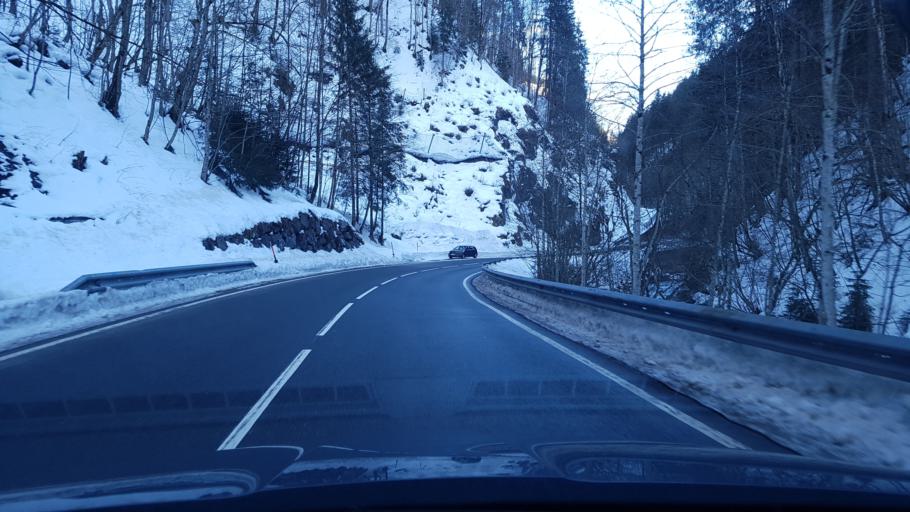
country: AT
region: Salzburg
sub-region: Politischer Bezirk Zell am See
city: Lend
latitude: 47.3332
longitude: 13.0204
